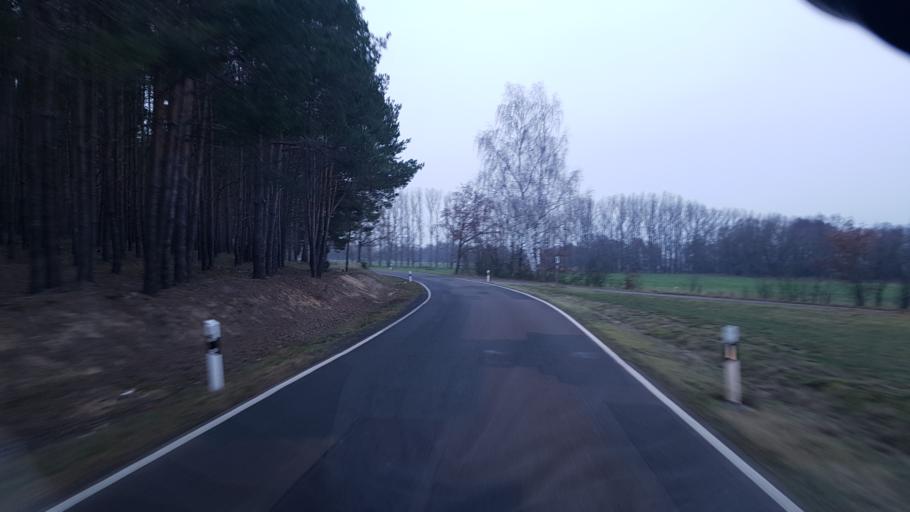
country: DE
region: Brandenburg
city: Briesen
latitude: 51.8519
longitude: 14.2311
